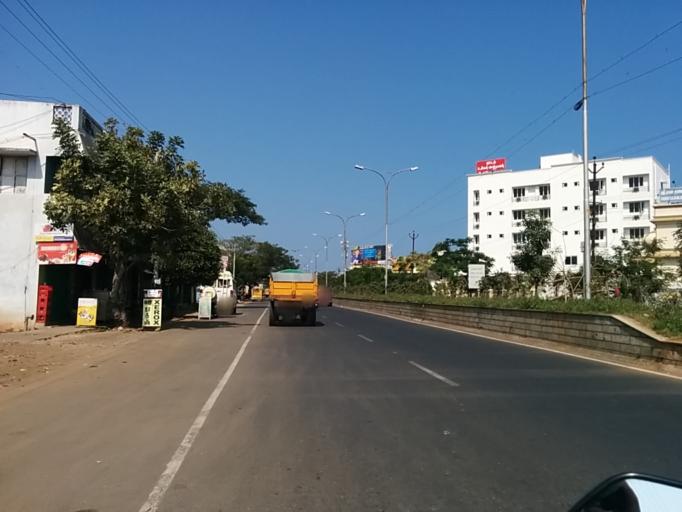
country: IN
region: Pondicherry
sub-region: Puducherry
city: Puducherry
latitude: 11.9467
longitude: 79.8113
